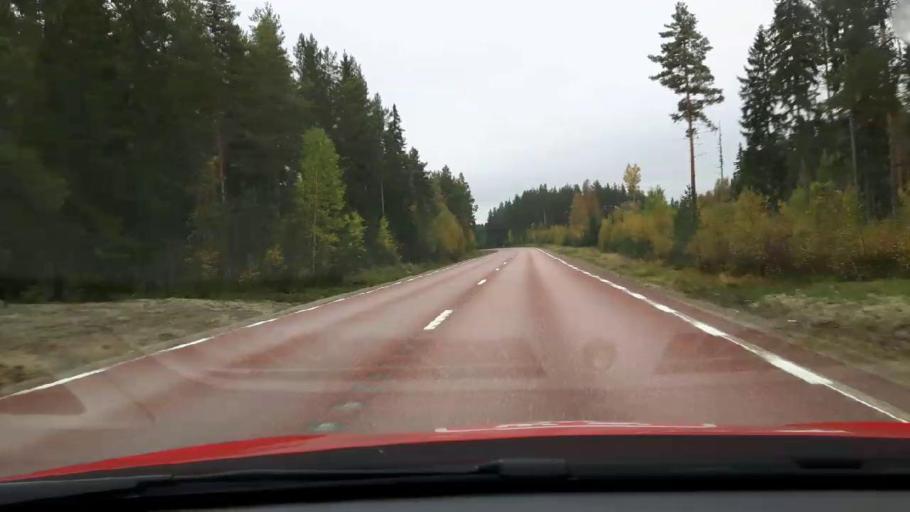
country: SE
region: Gaevleborg
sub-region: Ljusdals Kommun
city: Farila
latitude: 61.8232
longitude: 15.7562
